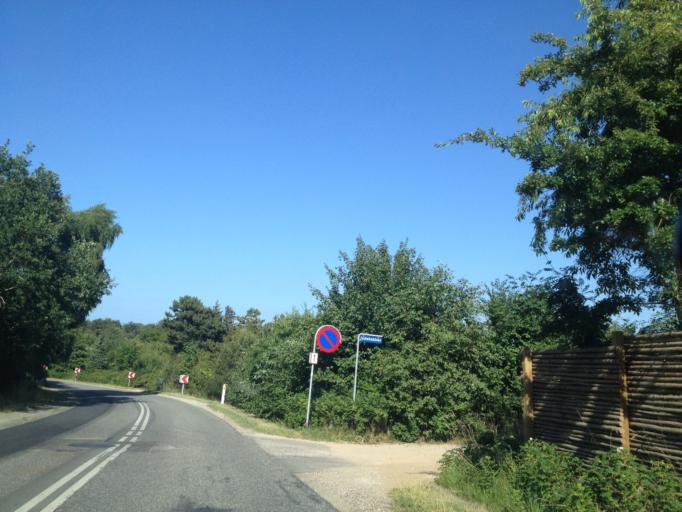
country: DK
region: Capital Region
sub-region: Gribskov Kommune
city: Helsinge
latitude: 56.0951
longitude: 12.1579
